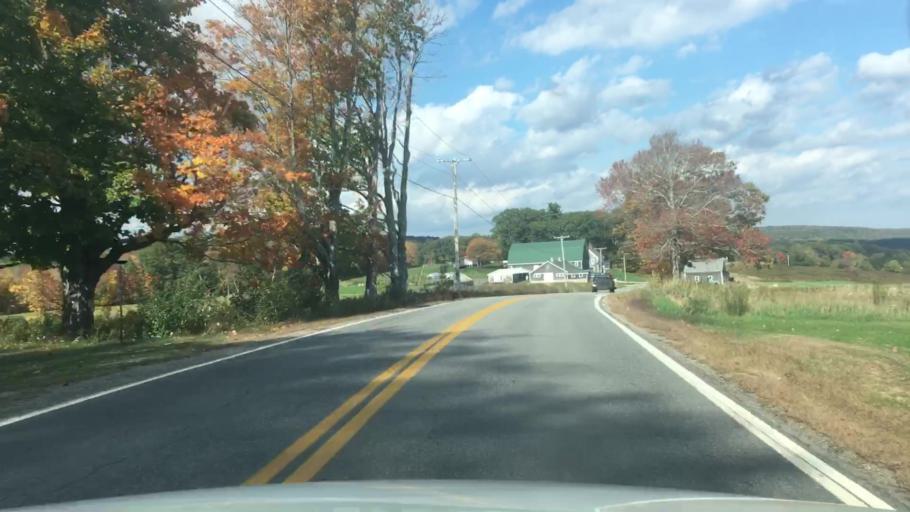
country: US
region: Maine
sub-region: Knox County
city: Appleton
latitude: 44.2589
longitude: -69.2764
